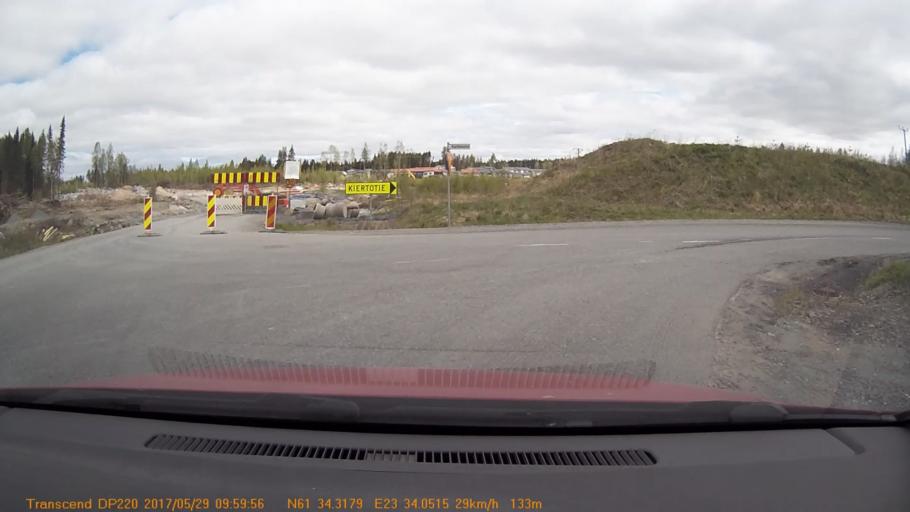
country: FI
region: Pirkanmaa
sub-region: Tampere
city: Yloejaervi
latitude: 61.5720
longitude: 23.5675
